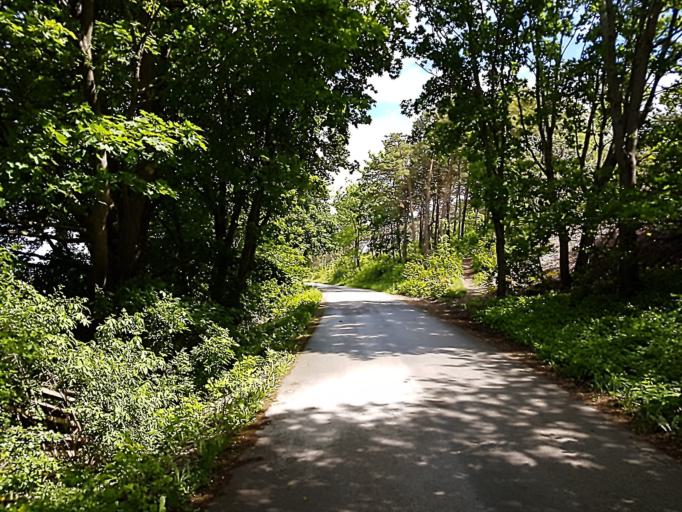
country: SE
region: Gotland
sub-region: Gotland
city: Visby
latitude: 57.7153
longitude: 18.3829
